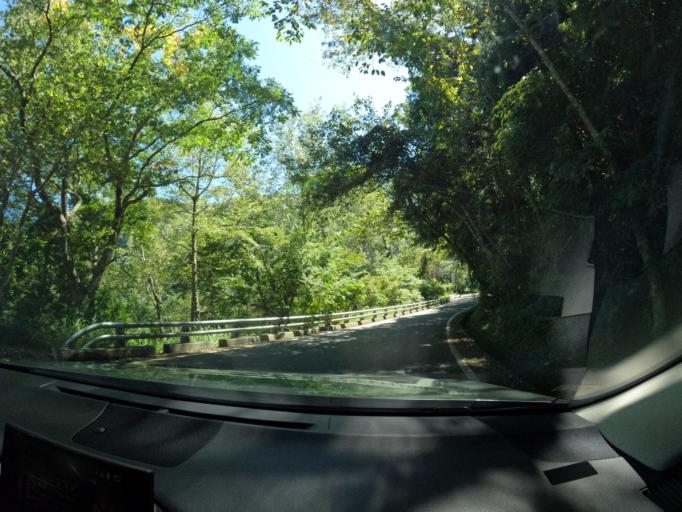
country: TW
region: Taiwan
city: Yujing
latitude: 23.2830
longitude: 120.8906
